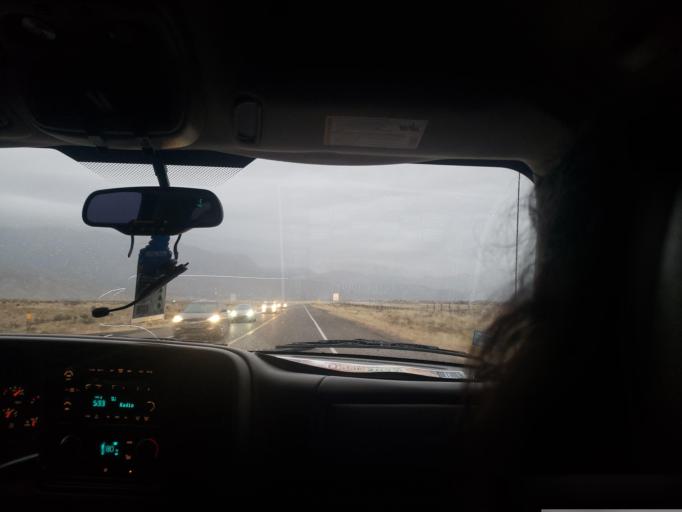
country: US
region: New Mexico
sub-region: Sandoval County
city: Corrales
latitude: 35.2023
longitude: -106.5541
